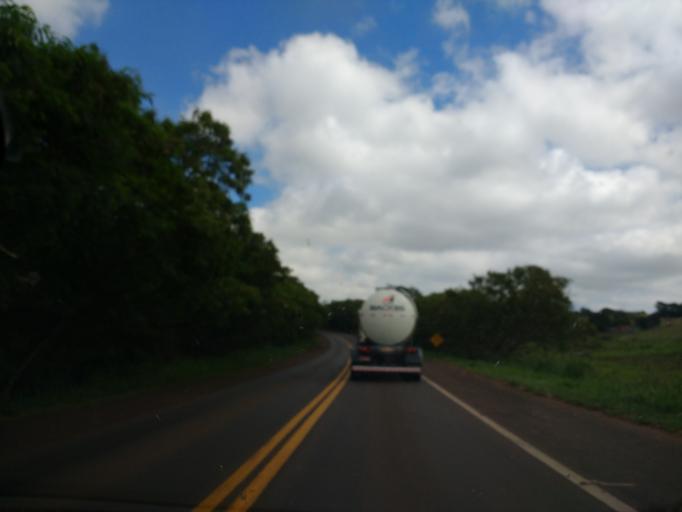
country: BR
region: Parana
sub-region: Cruzeiro Do Oeste
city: Cruzeiro do Oeste
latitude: -23.7893
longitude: -53.0329
